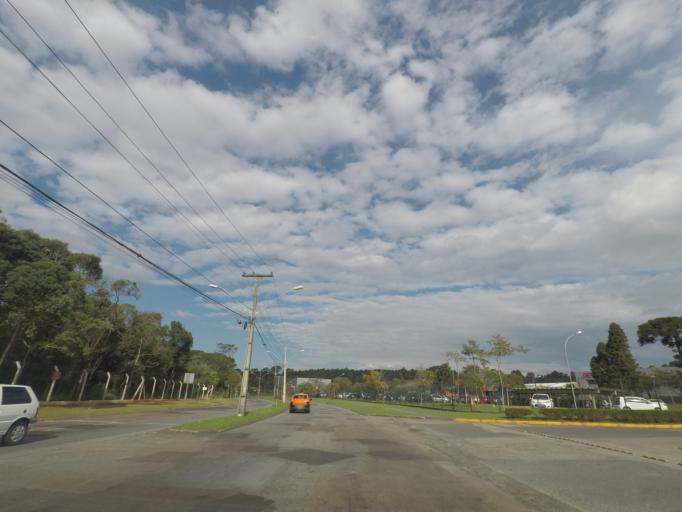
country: BR
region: Parana
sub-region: Sao Jose Dos Pinhais
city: Sao Jose dos Pinhais
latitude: -25.5333
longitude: -49.3078
